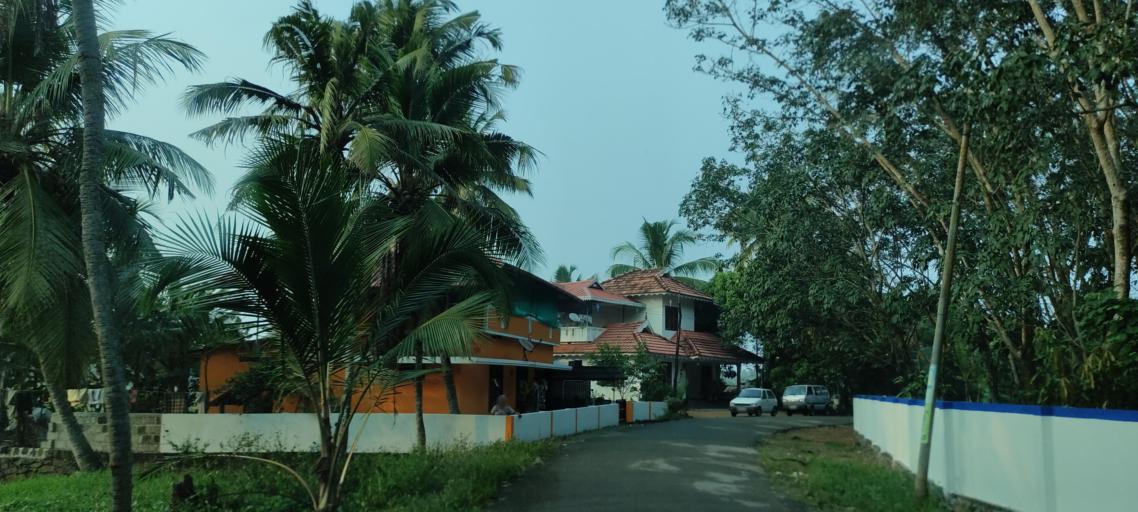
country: IN
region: Kerala
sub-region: Kottayam
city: Vaikam
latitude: 9.6808
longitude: 76.4645
